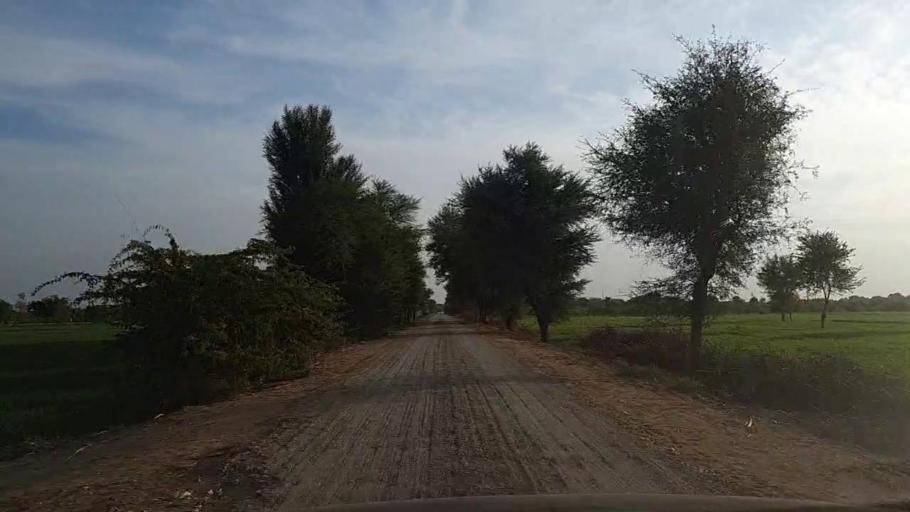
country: PK
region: Sindh
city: Jam Sahib
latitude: 26.4367
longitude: 68.5716
